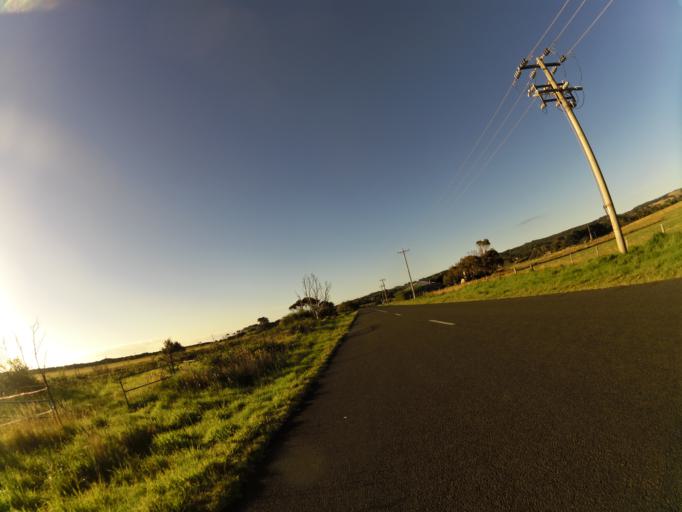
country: AU
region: Victoria
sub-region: Colac-Otway
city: Apollo Bay
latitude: -38.7644
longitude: 143.6614
